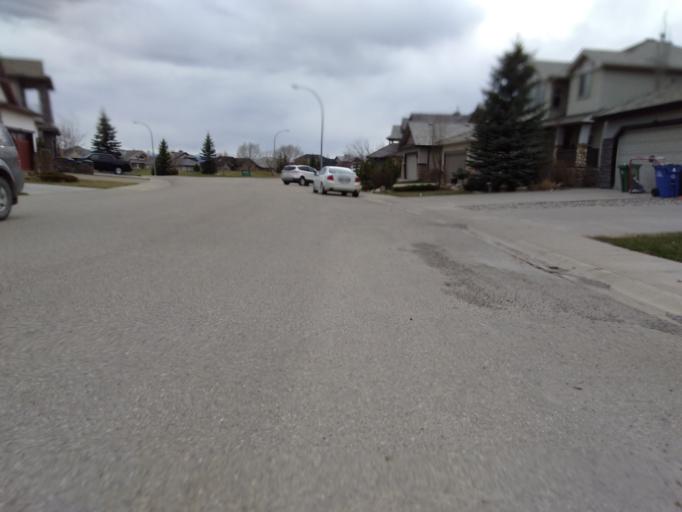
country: CA
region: Alberta
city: Cochrane
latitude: 51.1820
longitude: -114.4249
